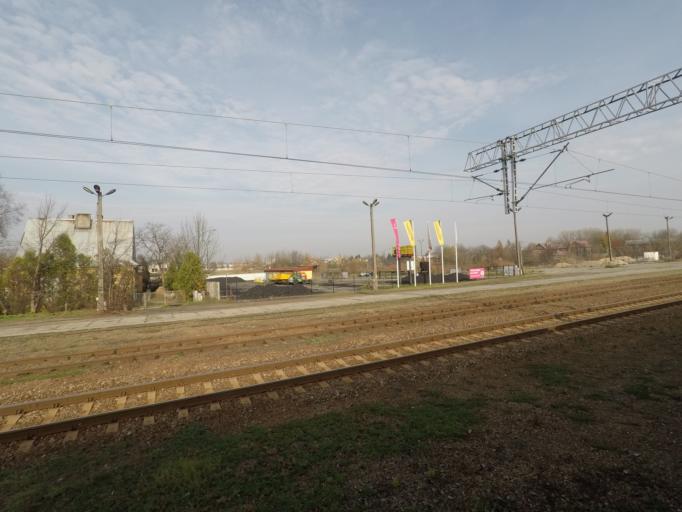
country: PL
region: Subcarpathian Voivodeship
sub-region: Powiat lancucki
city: Lancut
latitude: 50.0818
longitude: 22.2283
